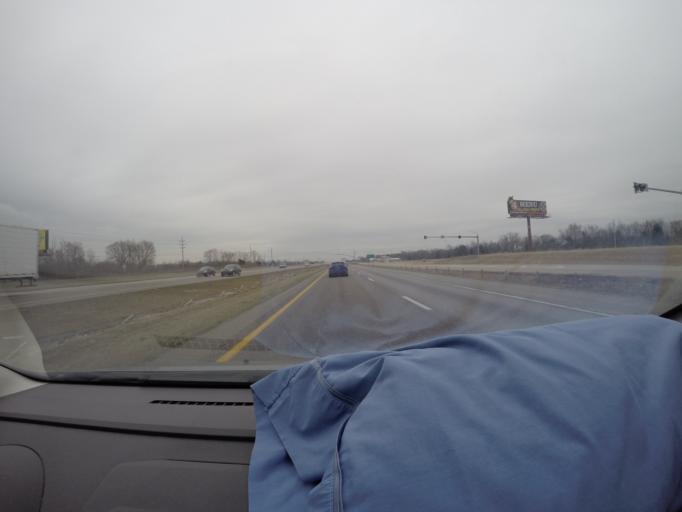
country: US
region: Missouri
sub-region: Warren County
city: Wright City
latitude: 38.8136
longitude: -90.9426
